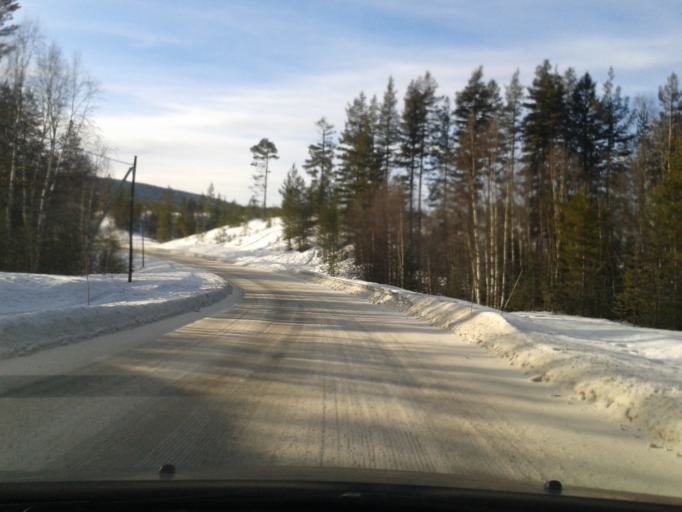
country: SE
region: Vaesternorrland
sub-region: OErnskoeldsviks Kommun
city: Bredbyn
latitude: 63.6752
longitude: 17.8113
